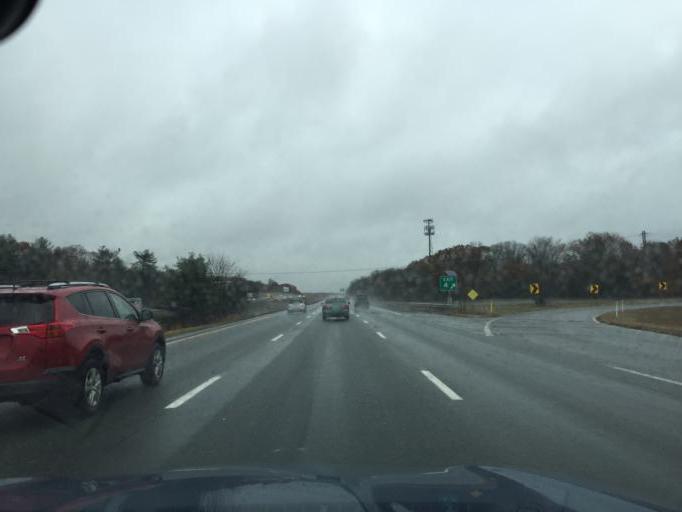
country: US
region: Massachusetts
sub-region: Bristol County
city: Attleboro
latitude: 41.9565
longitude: -71.3031
